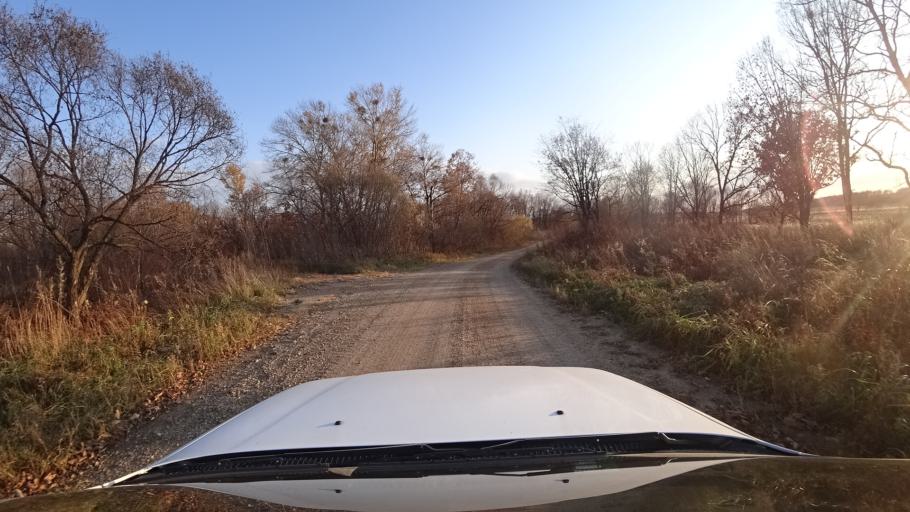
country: RU
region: Primorskiy
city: Lazo
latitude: 45.8163
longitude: 133.6112
